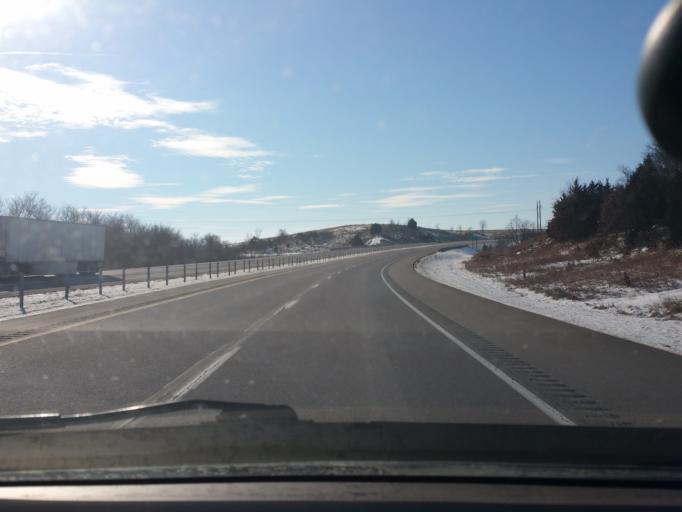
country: US
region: Iowa
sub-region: Clarke County
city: Osceola
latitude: 41.0547
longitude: -93.7819
